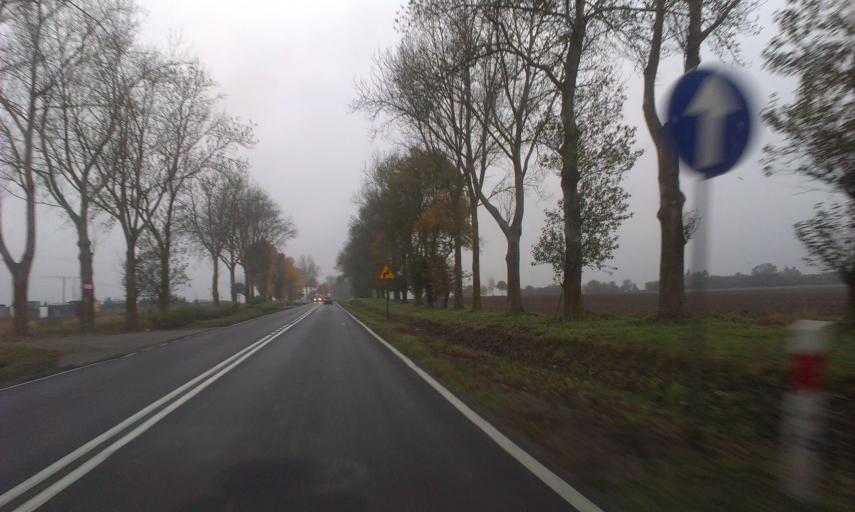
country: PL
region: West Pomeranian Voivodeship
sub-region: Koszalin
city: Koszalin
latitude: 54.1555
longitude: 16.2340
